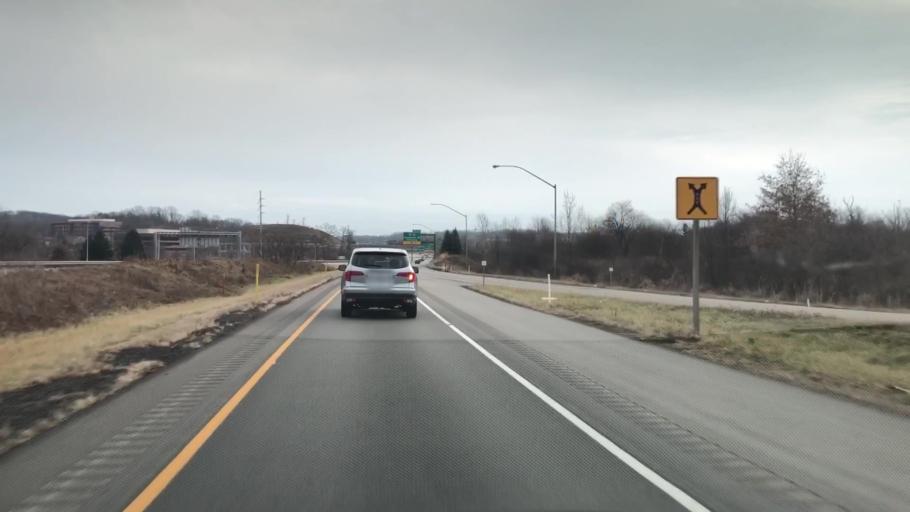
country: US
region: Pennsylvania
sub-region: Butler County
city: Cranberry Township
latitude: 40.6837
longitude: -80.0959
